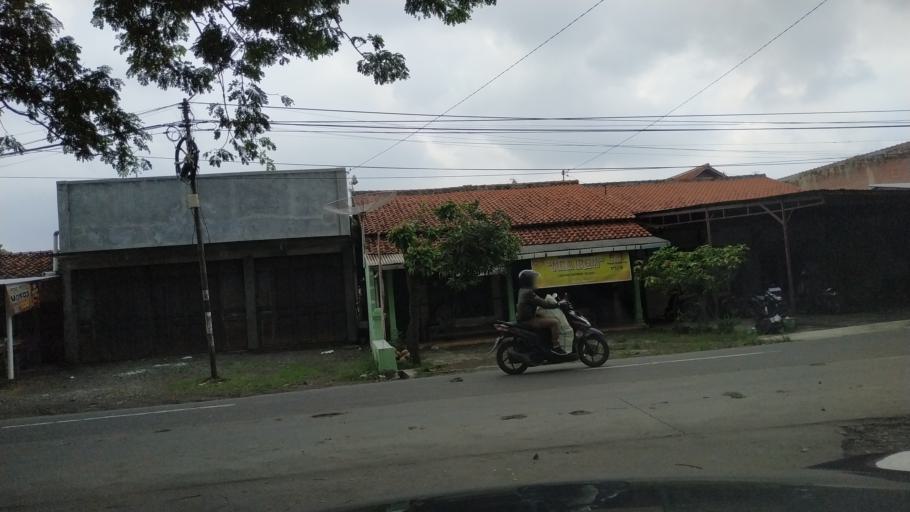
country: ID
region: Central Java
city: Slawi
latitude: -6.9907
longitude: 109.1210
